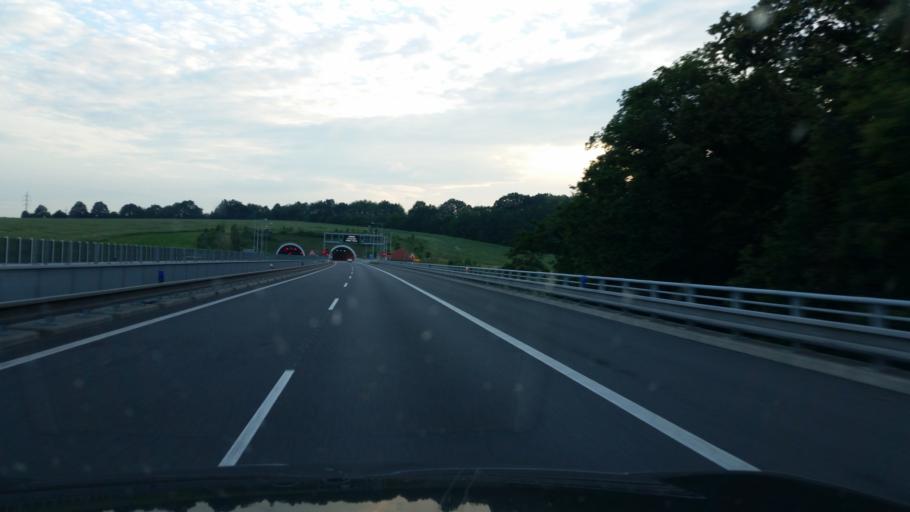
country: CZ
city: Klimkovice
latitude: 49.7973
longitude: 18.1277
